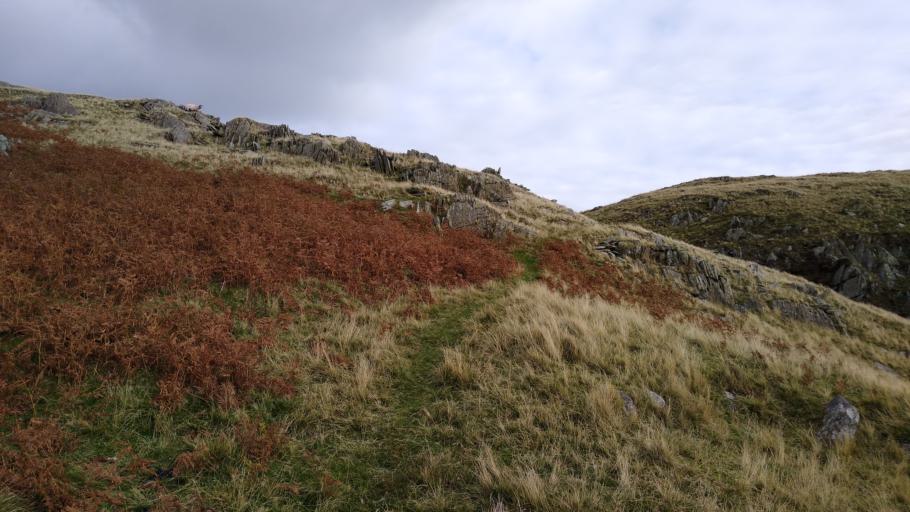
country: GB
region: England
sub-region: Cumbria
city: Ambleside
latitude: 54.3790
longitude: -3.0861
